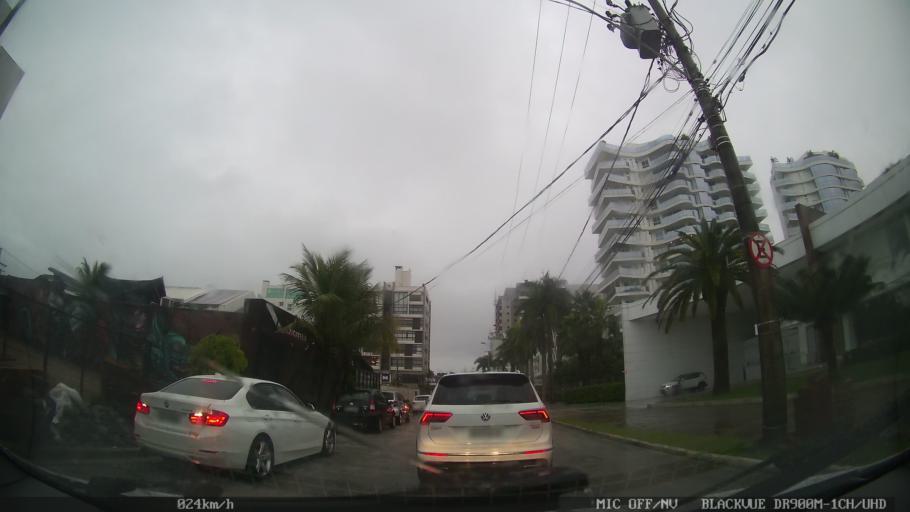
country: BR
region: Santa Catarina
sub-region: Balneario Camboriu
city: Balneario Camboriu
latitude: -26.9437
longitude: -48.6302
